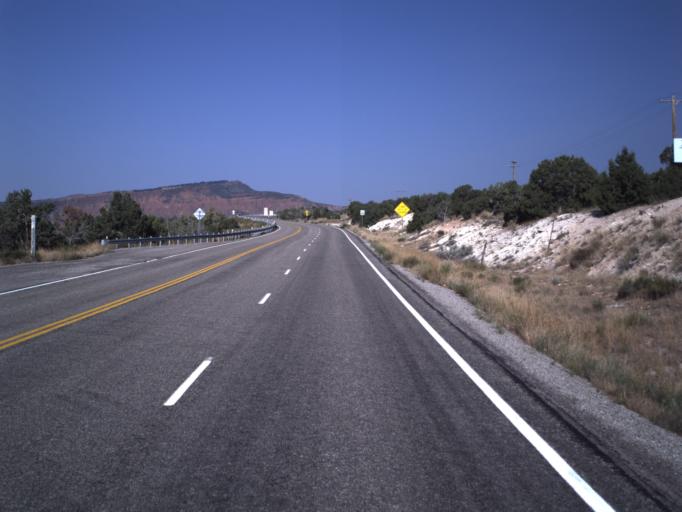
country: US
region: Utah
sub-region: Uintah County
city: Vernal
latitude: 40.6096
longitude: -109.4726
